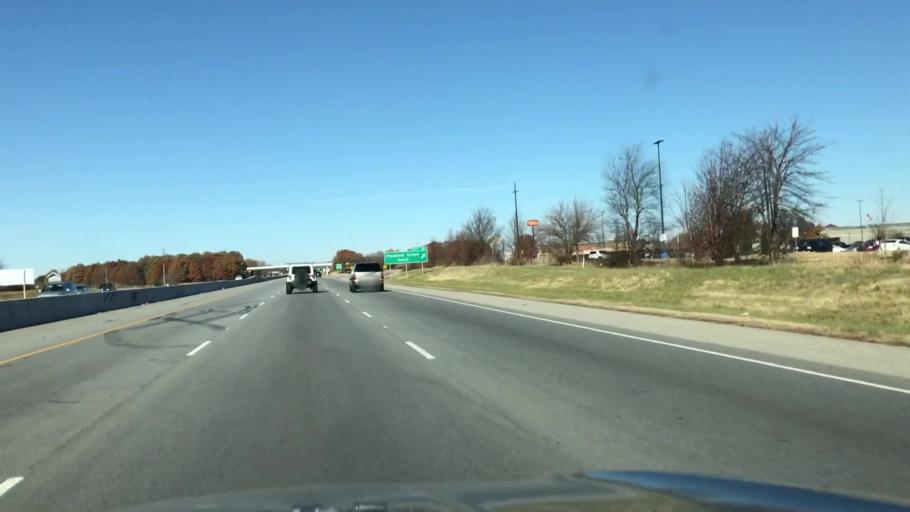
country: US
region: Arkansas
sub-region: Benton County
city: Lowell
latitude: 36.2784
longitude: -94.1525
